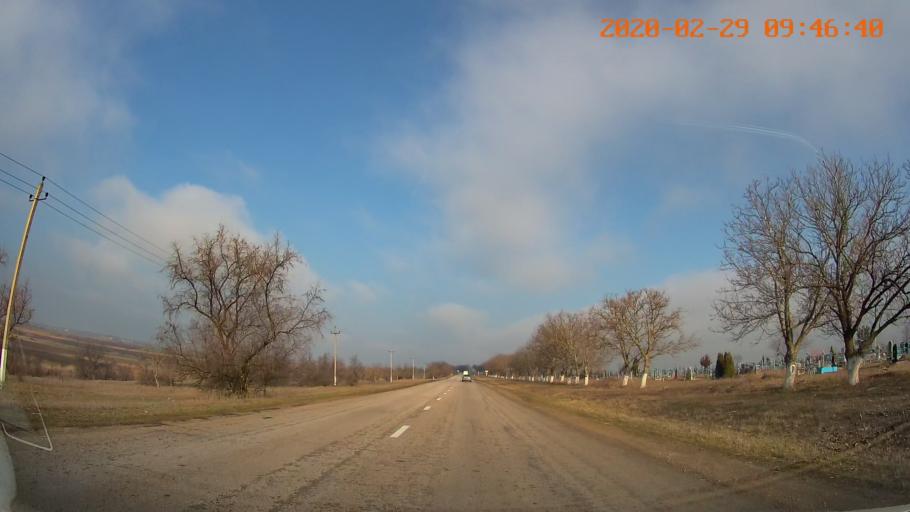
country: MD
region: Telenesti
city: Crasnoe
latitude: 46.6694
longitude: 29.7967
